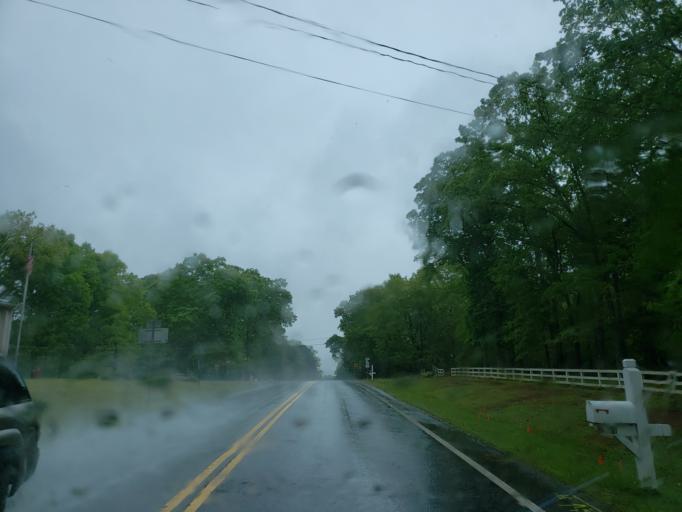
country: US
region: Georgia
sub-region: Carroll County
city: Temple
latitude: 33.7309
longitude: -85.0237
